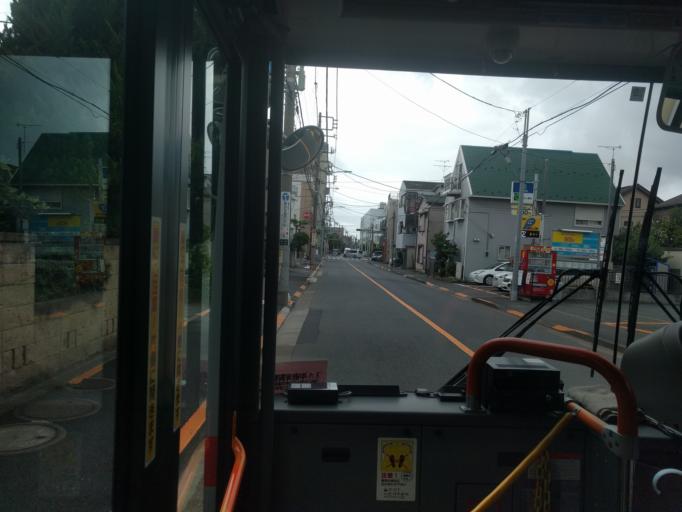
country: JP
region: Kanagawa
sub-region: Kawasaki-shi
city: Kawasaki
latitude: 35.5502
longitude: 139.7262
